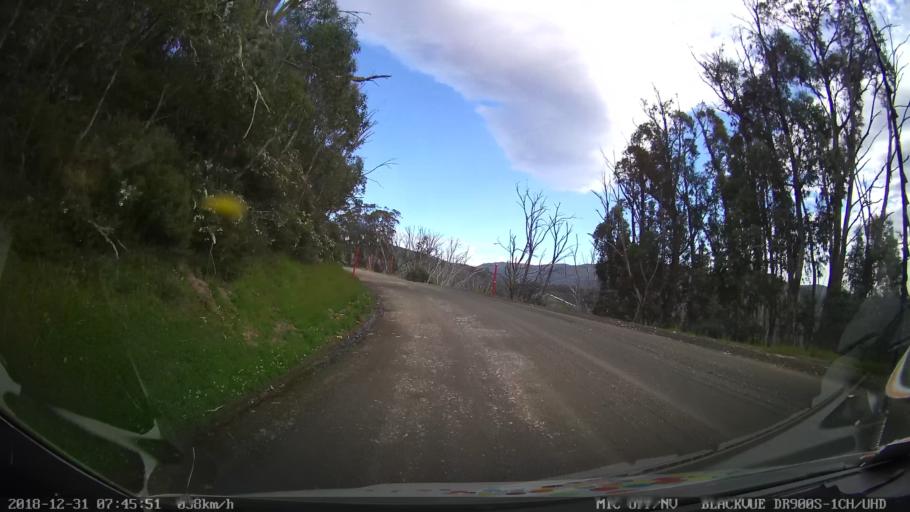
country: AU
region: New South Wales
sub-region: Snowy River
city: Jindabyne
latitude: -36.3617
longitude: 148.4034
